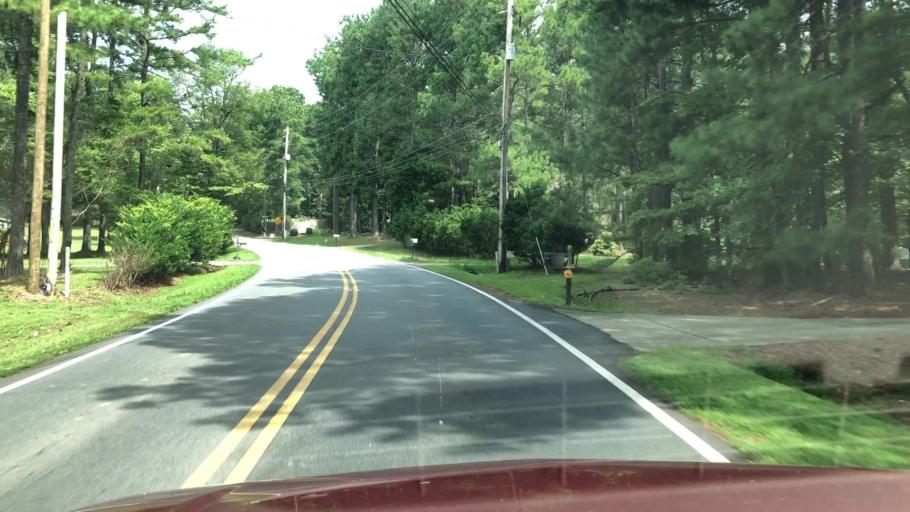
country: US
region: Georgia
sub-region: Cherokee County
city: Woodstock
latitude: 34.1500
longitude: -84.5937
